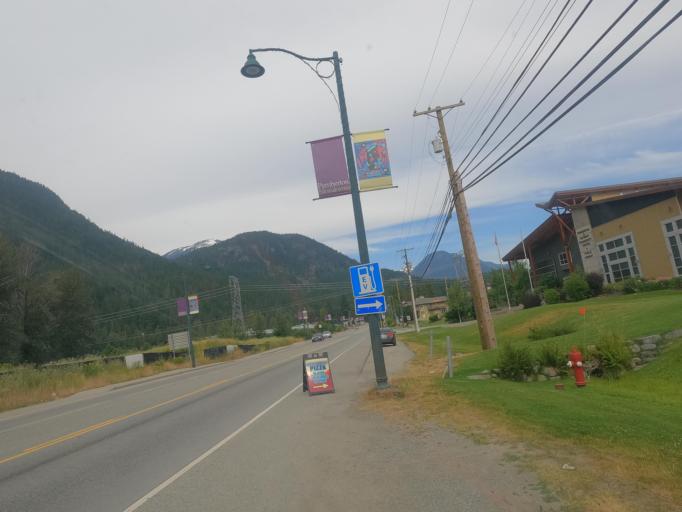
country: CA
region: British Columbia
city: Pemberton
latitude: 50.3183
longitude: -122.8000
